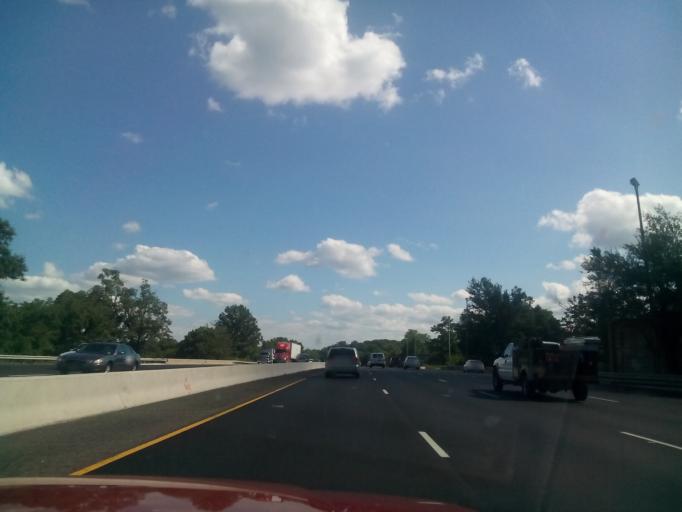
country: US
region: New Jersey
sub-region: Morris County
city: Rockaway
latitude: 40.8976
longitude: -74.4884
